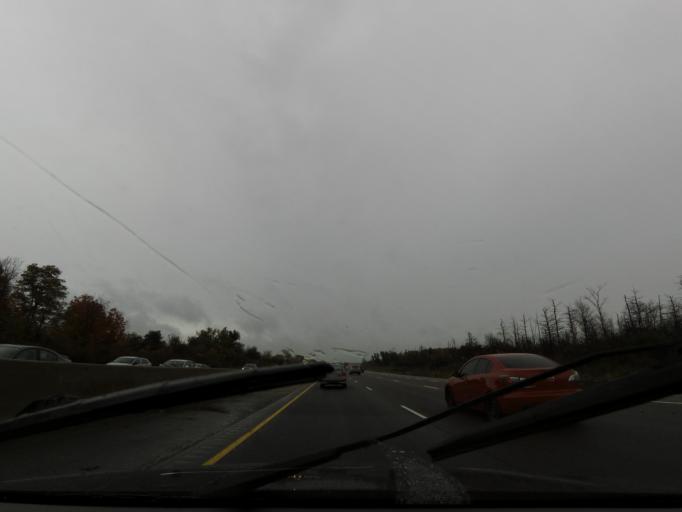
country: CA
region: Ontario
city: Cambridge
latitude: 43.4240
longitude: -80.2755
